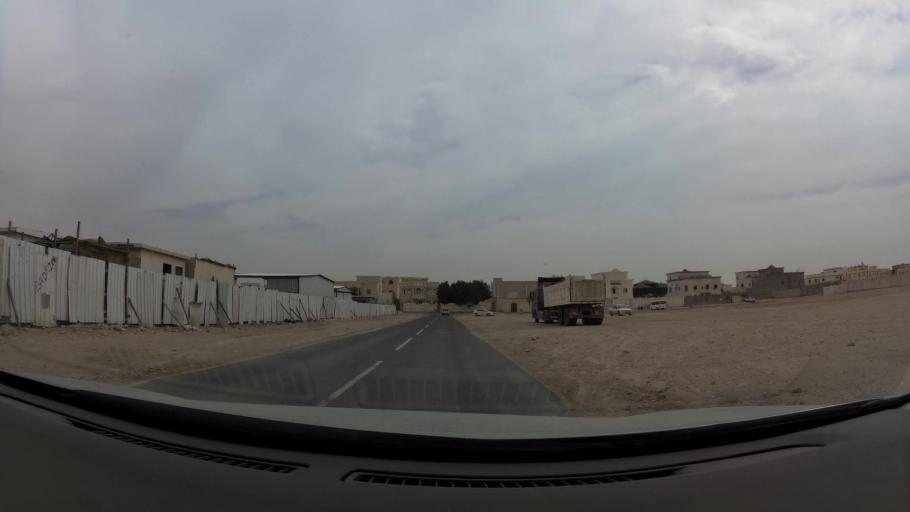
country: QA
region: Baladiyat ar Rayyan
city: Ar Rayyan
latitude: 25.2144
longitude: 51.4526
